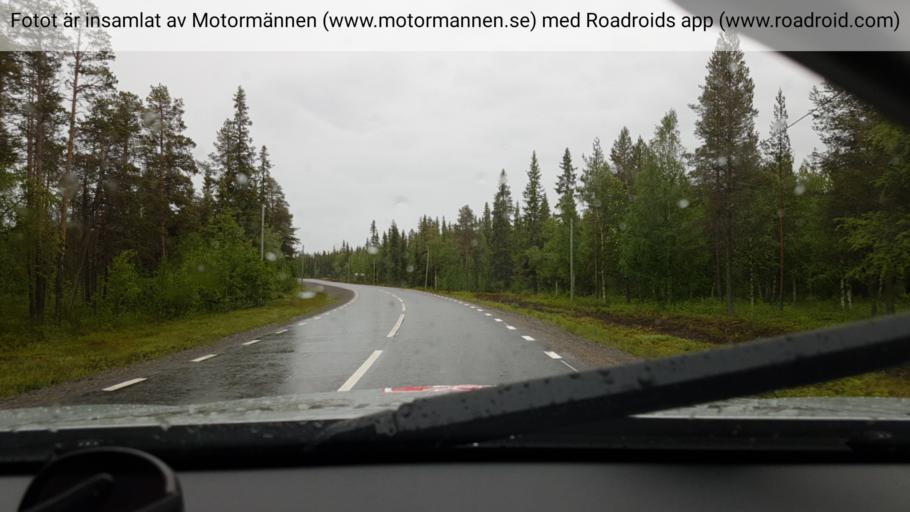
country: SE
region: Vaesterbotten
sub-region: Sorsele Kommun
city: Sorsele
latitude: 65.7930
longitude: 16.9801
